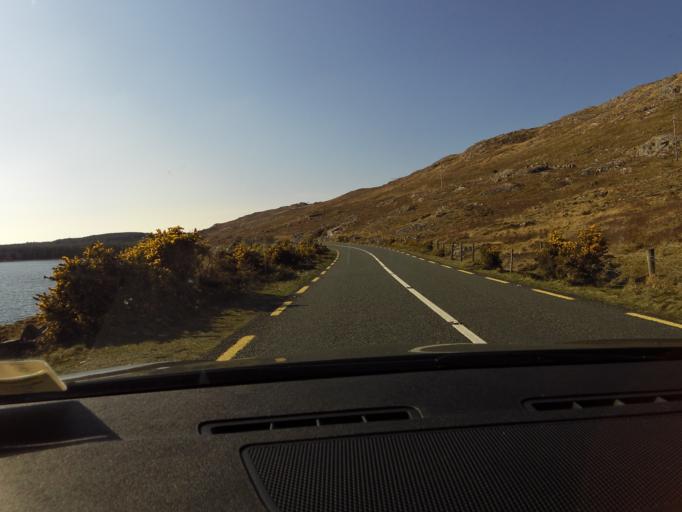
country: IE
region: Connaught
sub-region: County Galway
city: Clifden
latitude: 53.4711
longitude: -9.8586
